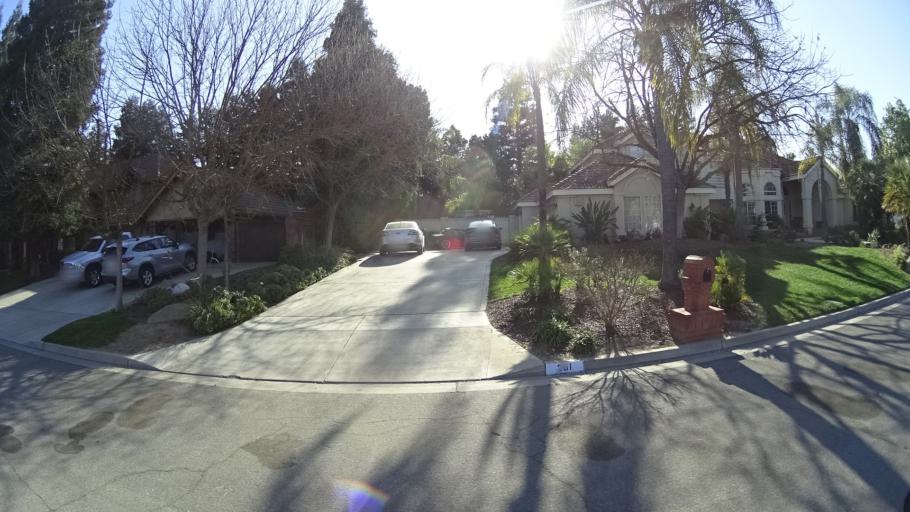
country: US
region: California
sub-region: Fresno County
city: Clovis
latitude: 36.8640
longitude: -119.7962
